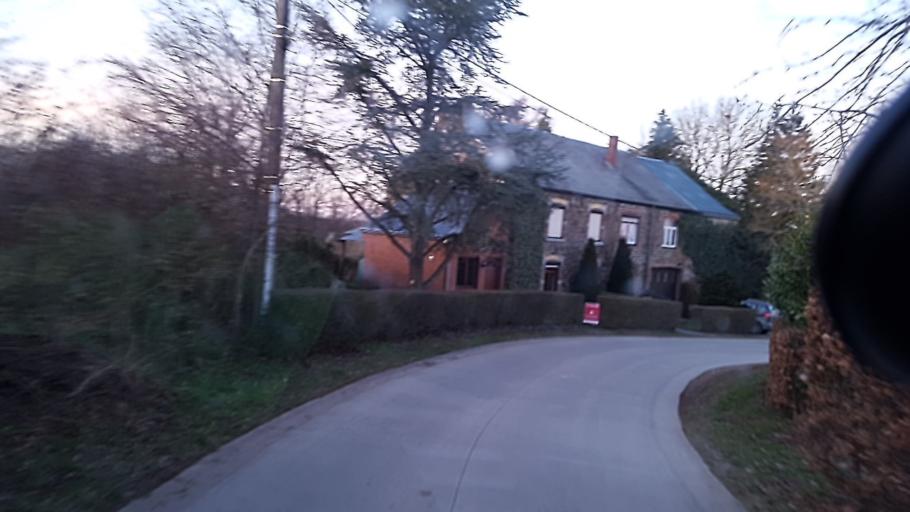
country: BE
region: Wallonia
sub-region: Province du Luxembourg
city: Wellin
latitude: 50.0685
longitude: 5.0756
